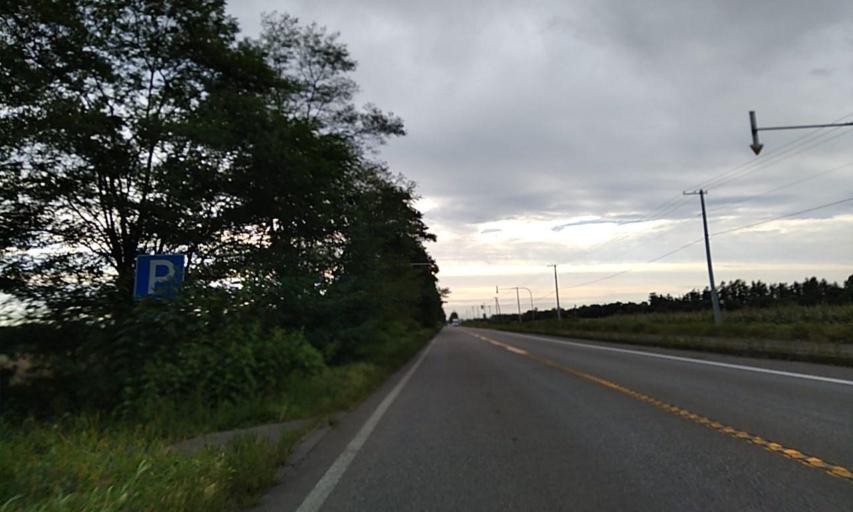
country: JP
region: Hokkaido
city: Obihiro
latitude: 42.9310
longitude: 142.9784
